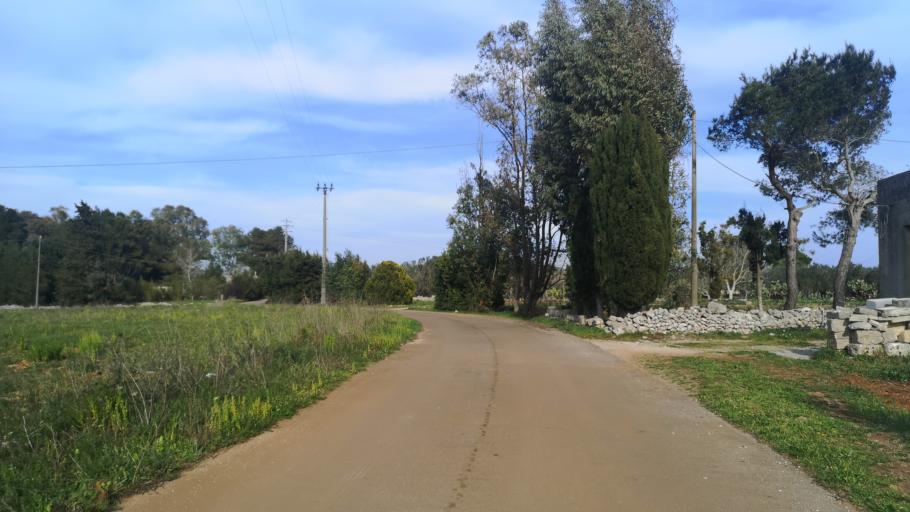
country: IT
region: Apulia
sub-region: Provincia di Lecce
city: Spongano
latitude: 40.0273
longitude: 18.3739
